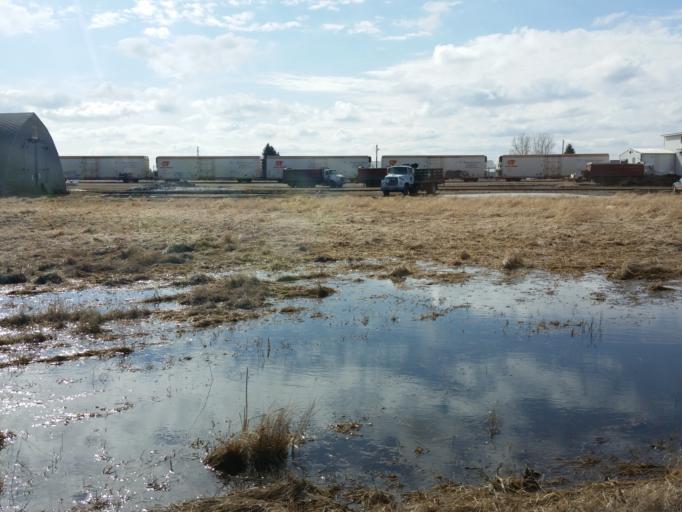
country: US
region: North Dakota
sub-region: Walsh County
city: Grafton
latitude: 48.4318
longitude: -97.4115
